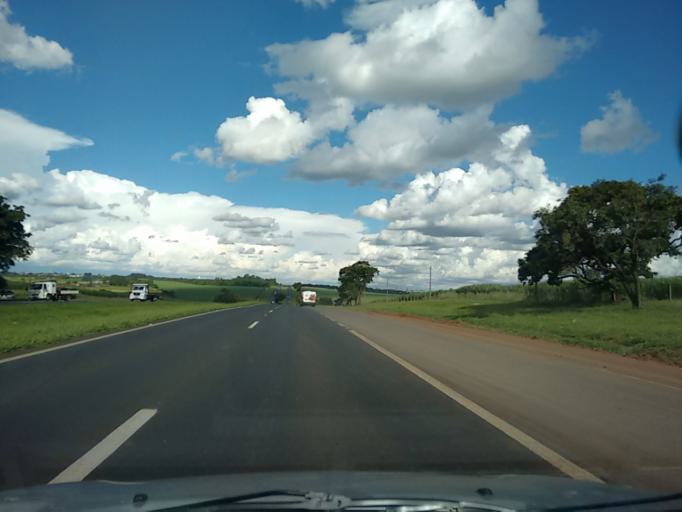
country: BR
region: Sao Paulo
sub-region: Ibate
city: Ibate
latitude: -21.9662
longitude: -47.9654
